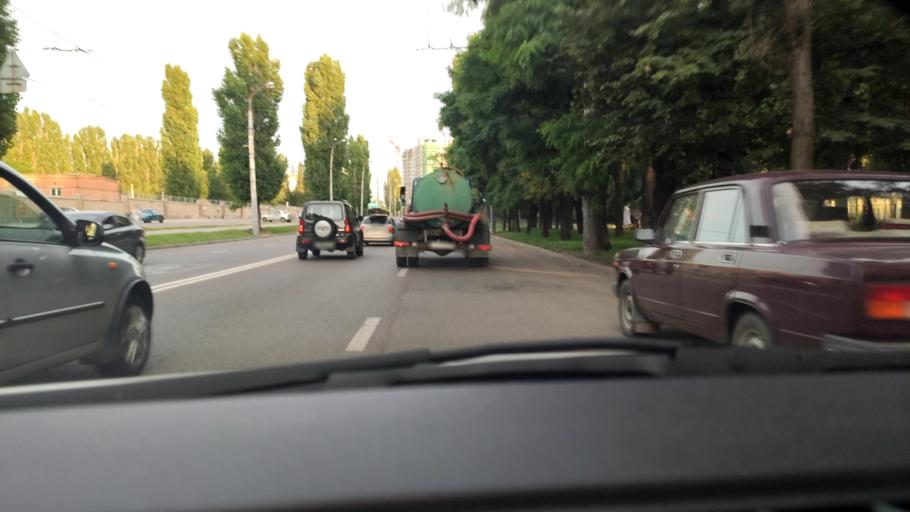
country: RU
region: Voronezj
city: Voronezh
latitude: 51.6537
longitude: 39.1609
